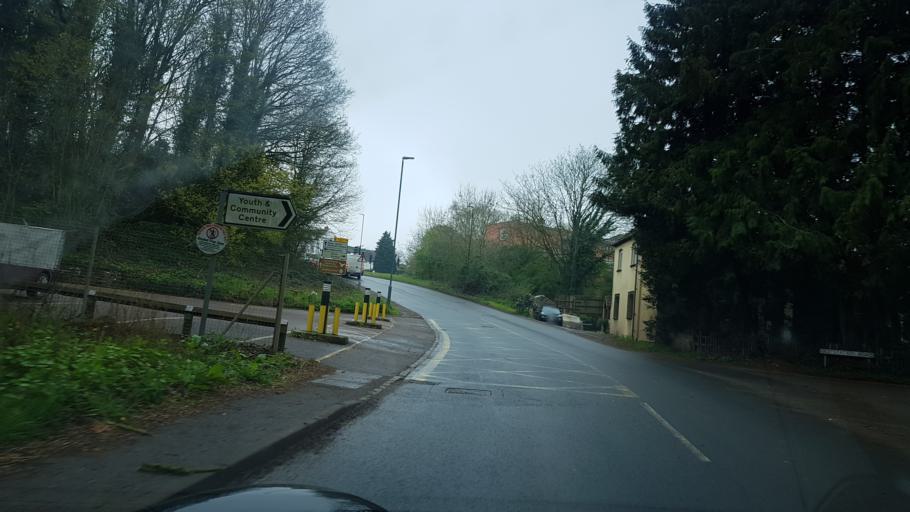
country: GB
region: England
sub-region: Gloucestershire
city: Newent
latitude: 51.9347
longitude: -2.4076
